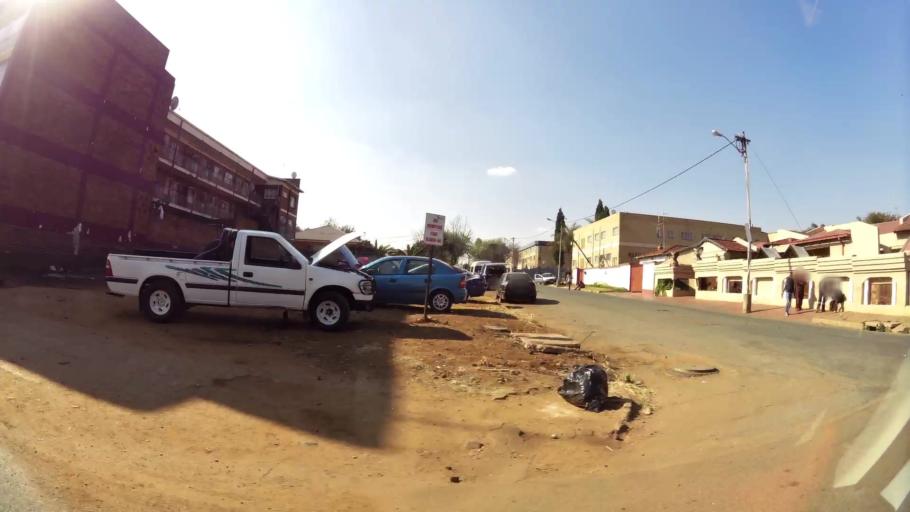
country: ZA
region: Gauteng
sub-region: City of Johannesburg Metropolitan Municipality
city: Modderfontein
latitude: -26.1119
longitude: 28.2317
